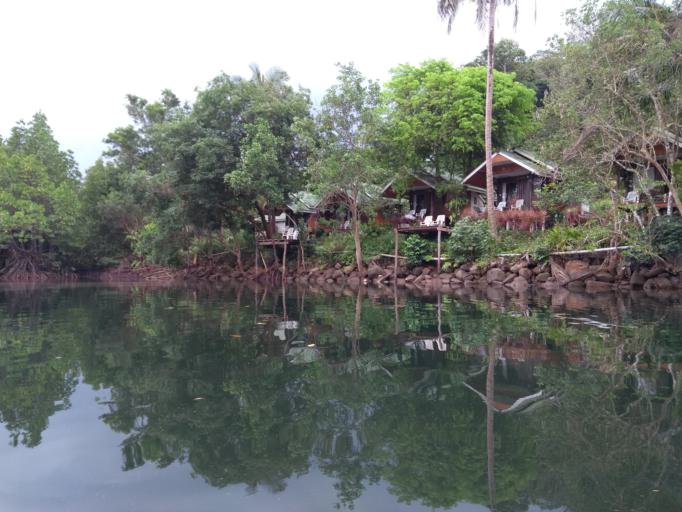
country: TH
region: Trat
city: Ko Kut
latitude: 11.6343
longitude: 102.5495
